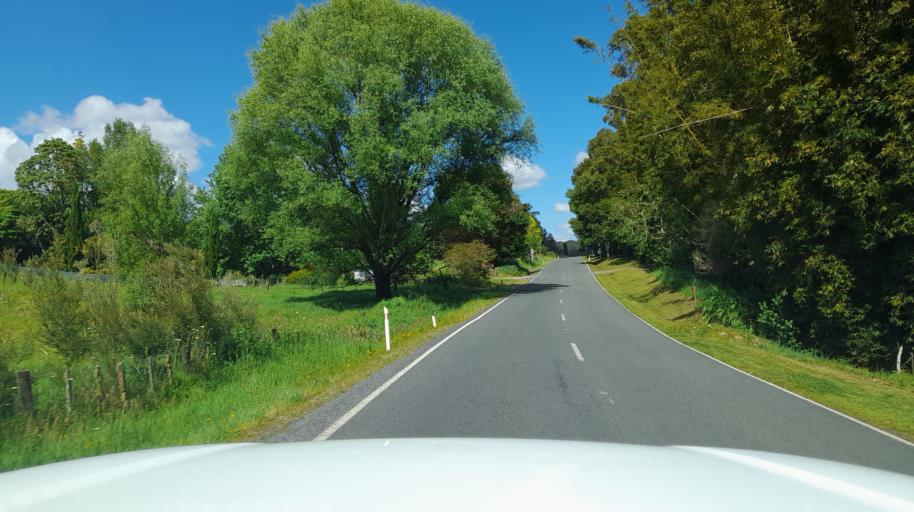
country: NZ
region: Northland
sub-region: Far North District
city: Taipa
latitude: -35.0931
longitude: 173.4981
